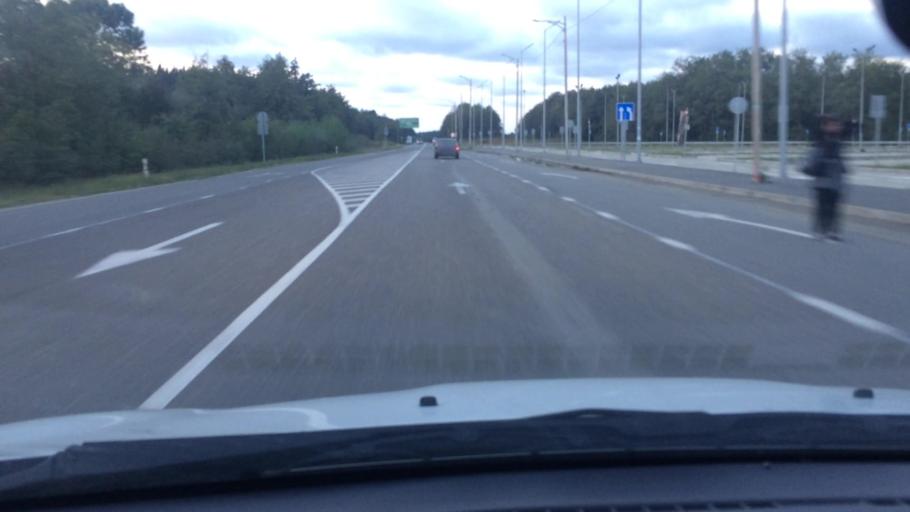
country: GE
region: Guria
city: Urek'i
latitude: 41.9391
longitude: 41.7714
